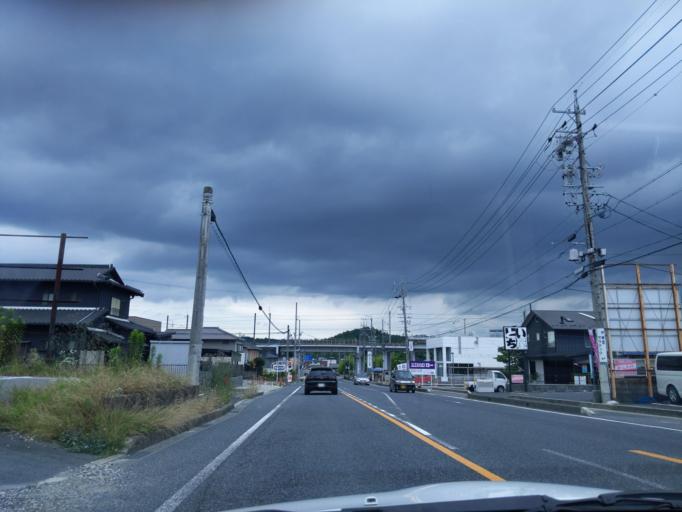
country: JP
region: Aichi
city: Seto
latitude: 35.1989
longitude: 137.1030
